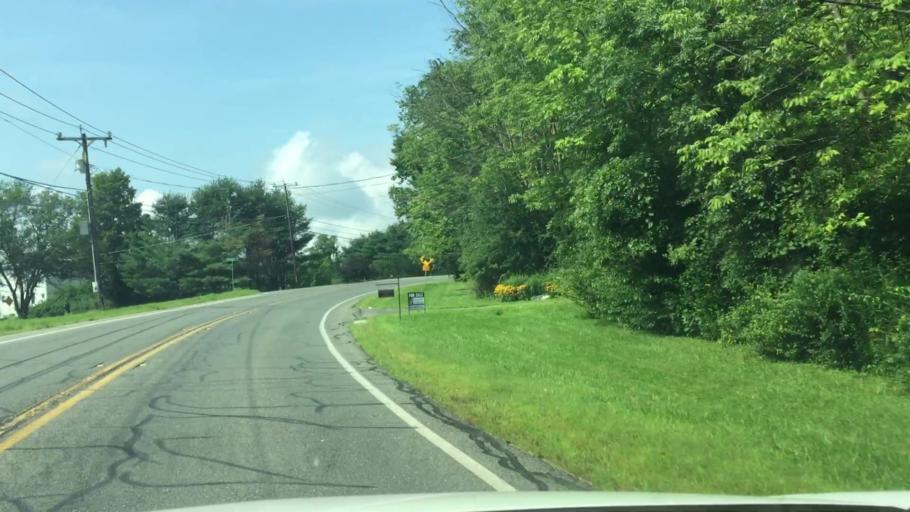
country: US
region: Massachusetts
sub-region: Berkshire County
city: Richmond
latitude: 42.4108
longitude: -73.3413
